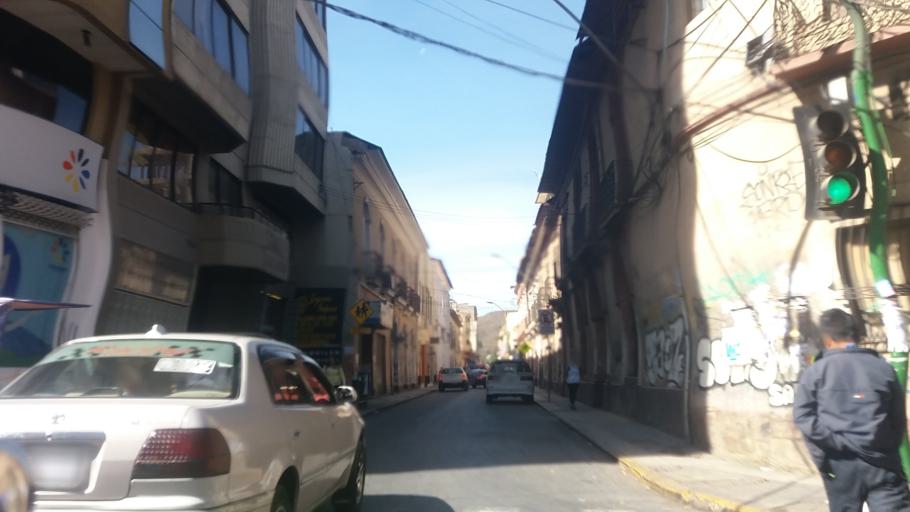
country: BO
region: Cochabamba
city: Cochabamba
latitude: -17.3939
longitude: -66.1542
